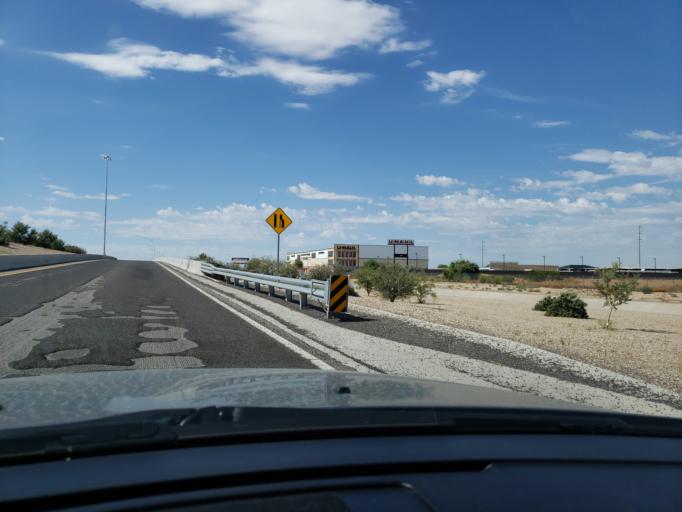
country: US
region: Arizona
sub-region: Maricopa County
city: Citrus Park
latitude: 33.5507
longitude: -112.4189
